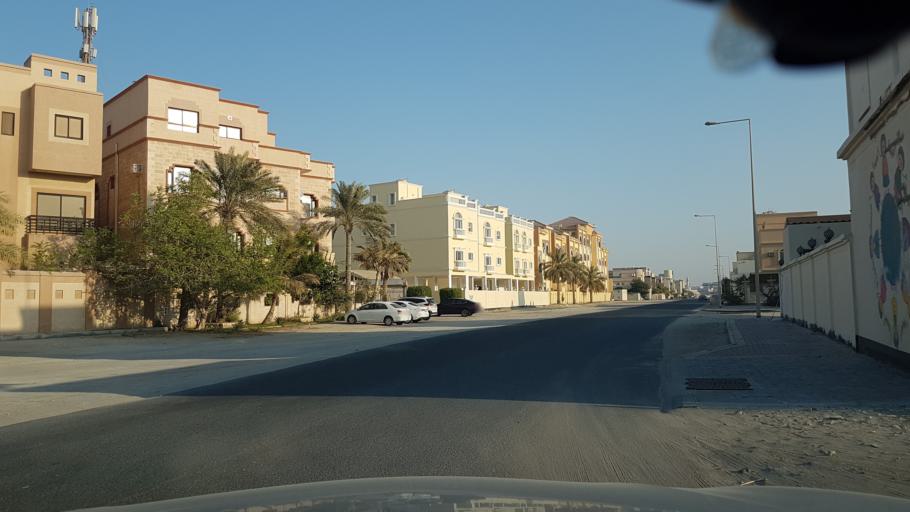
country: BH
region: Muharraq
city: Al Muharraq
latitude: 26.2791
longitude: 50.6030
